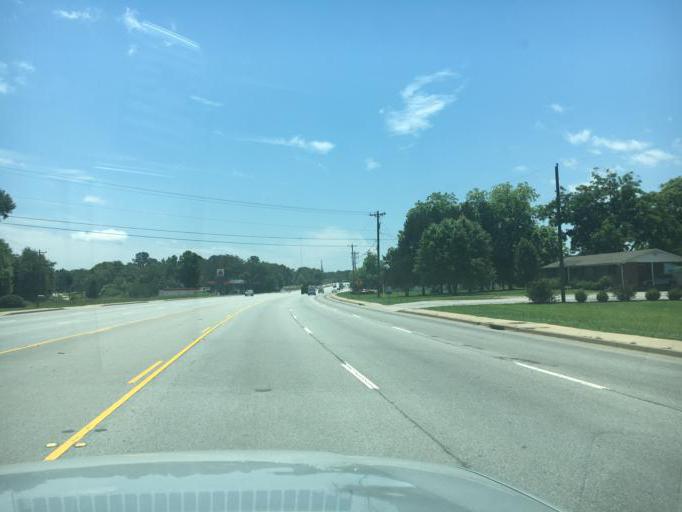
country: US
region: South Carolina
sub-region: Greenville County
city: Berea
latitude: 34.9070
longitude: -82.4608
